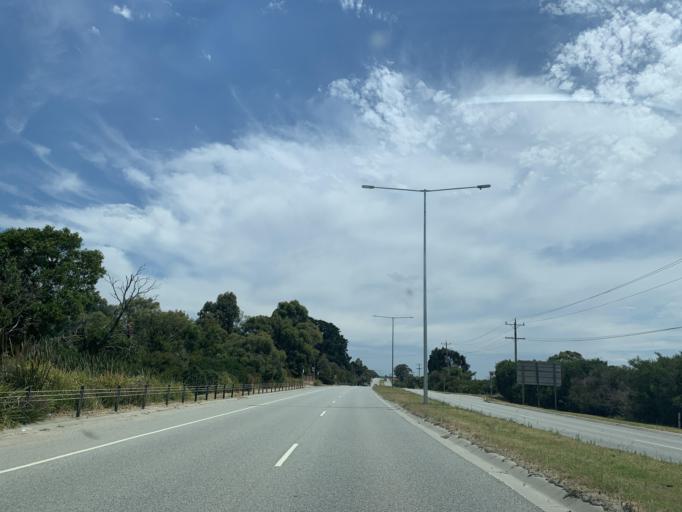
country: AU
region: Victoria
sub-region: Casey
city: Cranbourne South
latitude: -38.1249
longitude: 145.2478
